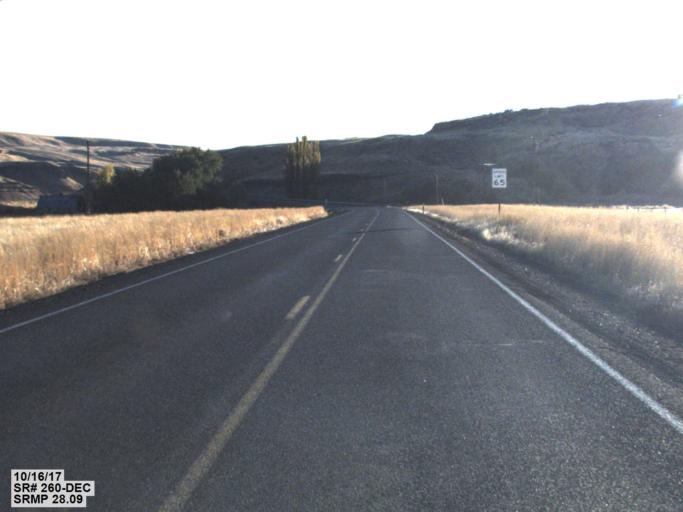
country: US
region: Washington
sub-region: Franklin County
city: Connell
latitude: 46.6577
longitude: -118.4948
